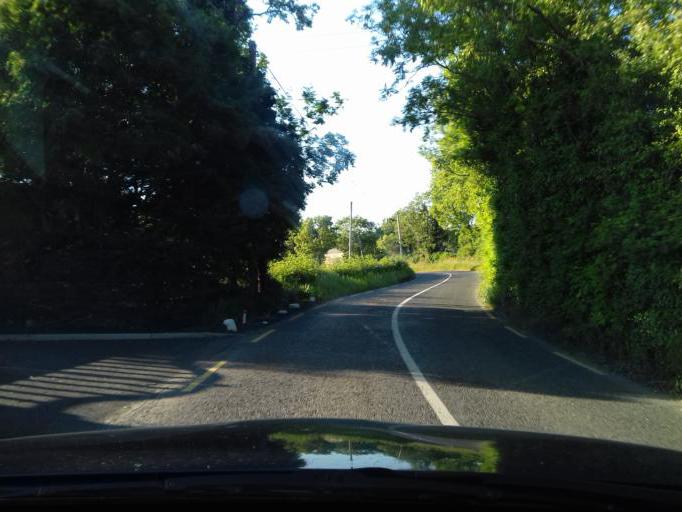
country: IE
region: Leinster
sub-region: An Mhi
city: Ashbourne
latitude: 53.5490
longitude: -6.3752
